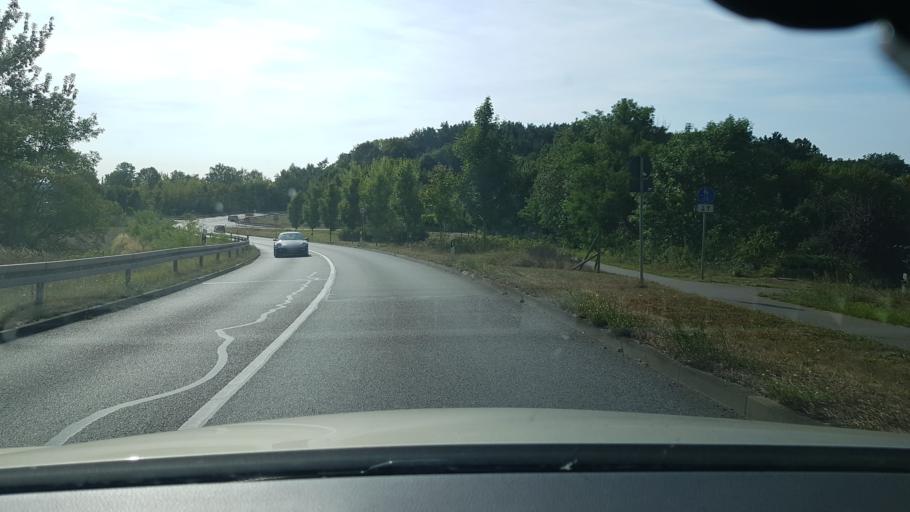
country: DE
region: Brandenburg
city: Lawitz
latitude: 52.1085
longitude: 14.6464
